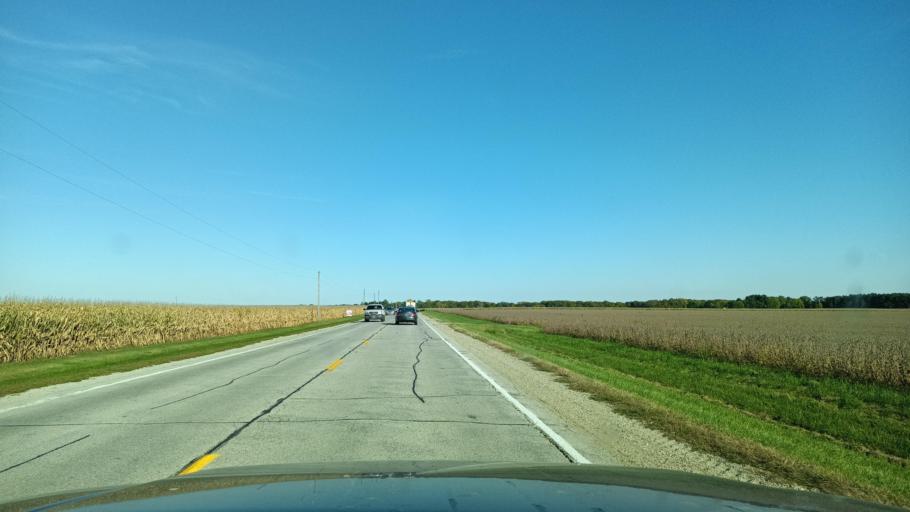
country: US
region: Illinois
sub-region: De Witt County
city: Farmer City
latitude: 40.2240
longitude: -88.7125
